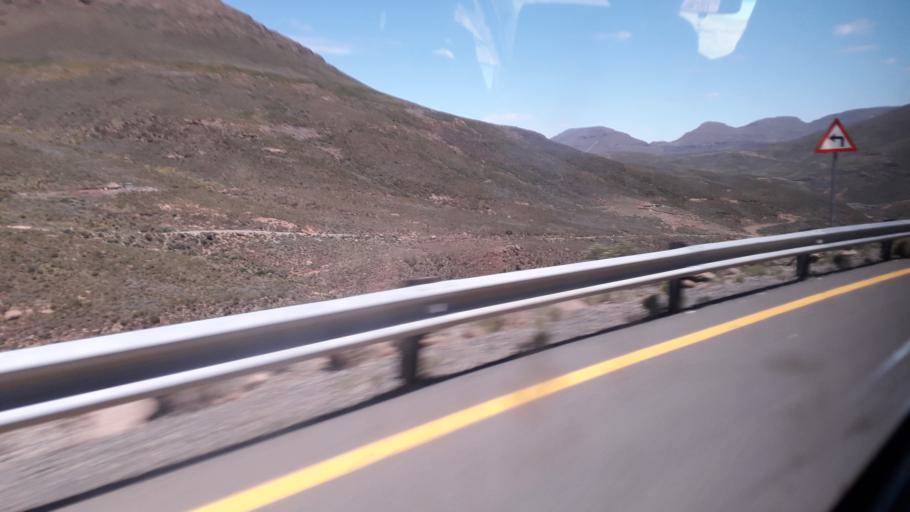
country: ZA
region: Orange Free State
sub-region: Thabo Mofutsanyana District Municipality
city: Phuthaditjhaba
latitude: -28.7706
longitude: 28.6661
